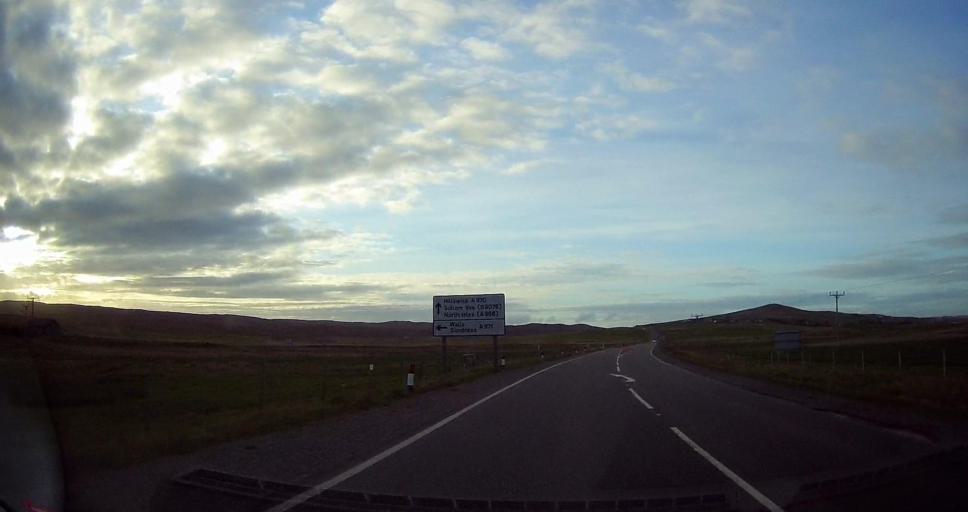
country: GB
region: Scotland
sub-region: Shetland Islands
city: Lerwick
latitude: 60.1894
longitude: -1.2319
